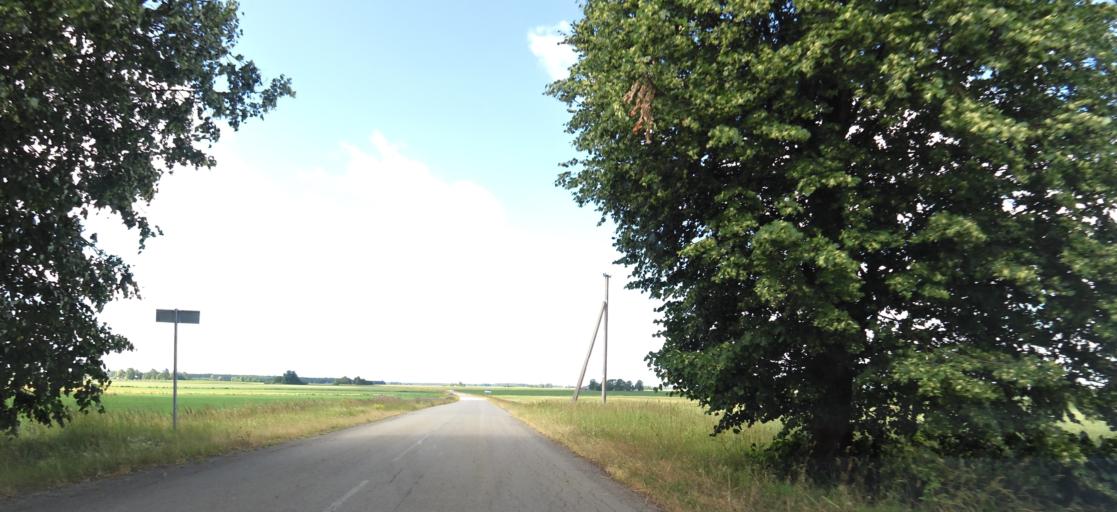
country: LT
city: Vabalninkas
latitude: 56.0615
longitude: 24.8285
